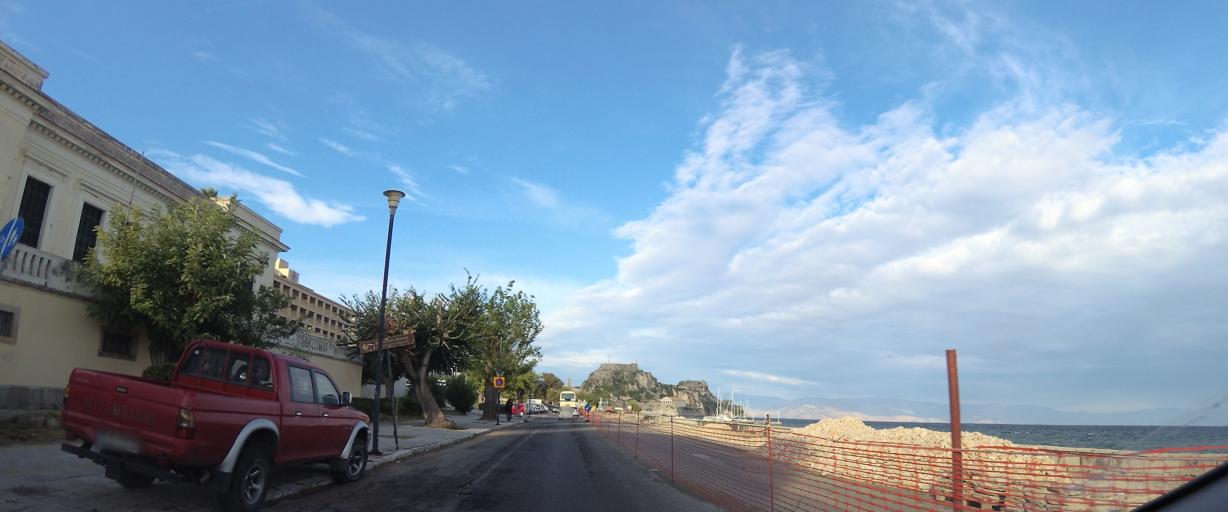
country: GR
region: Ionian Islands
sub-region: Nomos Kerkyras
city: Kerkyra
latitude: 39.6183
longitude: 19.9225
